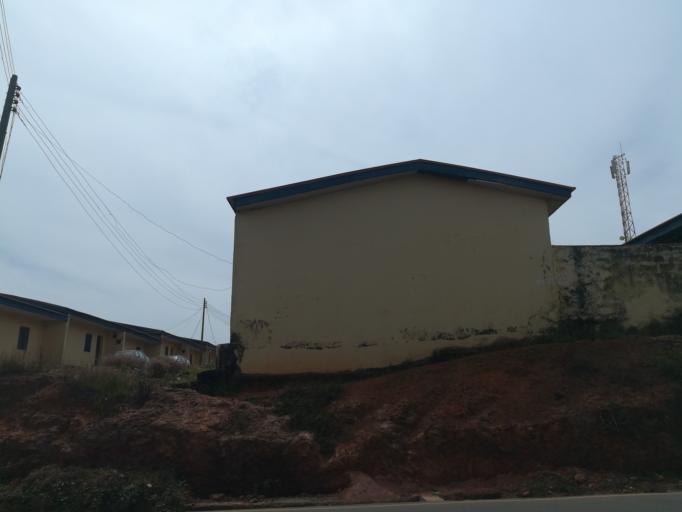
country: NG
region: Plateau
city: Jos
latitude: 9.8685
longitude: 8.8520
